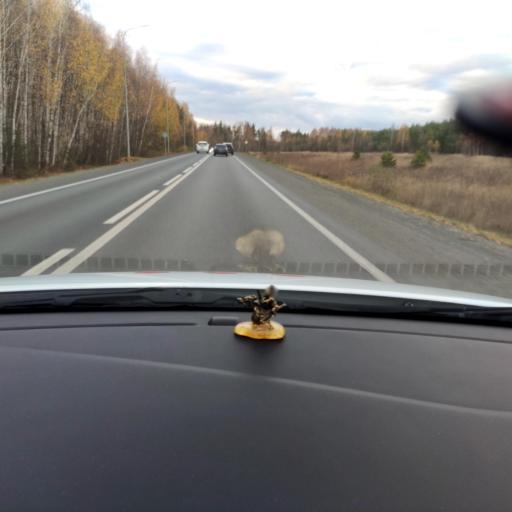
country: RU
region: Tatarstan
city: Stolbishchi
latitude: 55.6362
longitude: 49.1262
